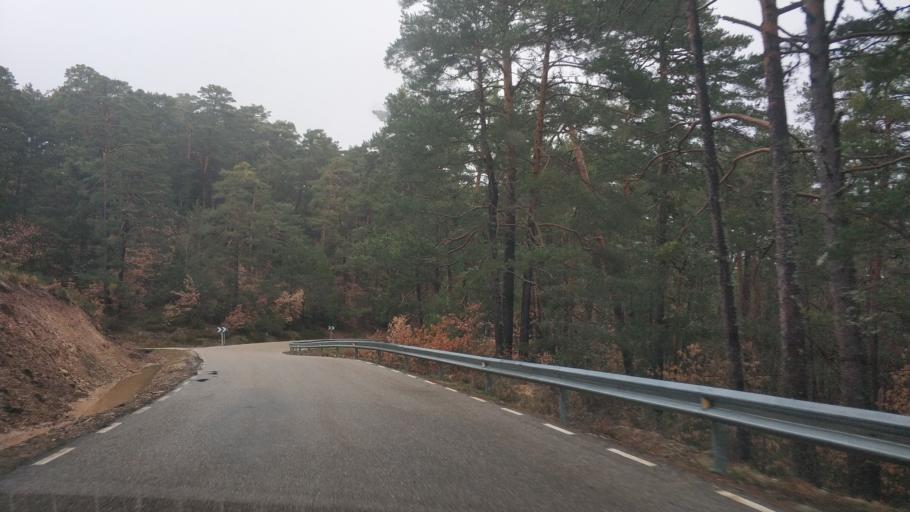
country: ES
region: Castille and Leon
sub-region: Provincia de Burgos
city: Quintanar de la Sierra
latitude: 42.0091
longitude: -3.0200
